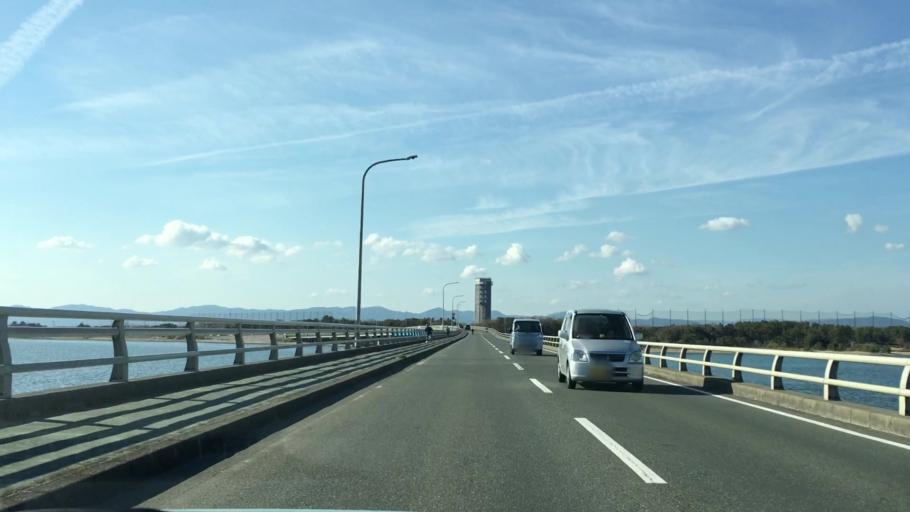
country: JP
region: Shizuoka
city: Kosai-shi
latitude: 34.7094
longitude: 137.6080
